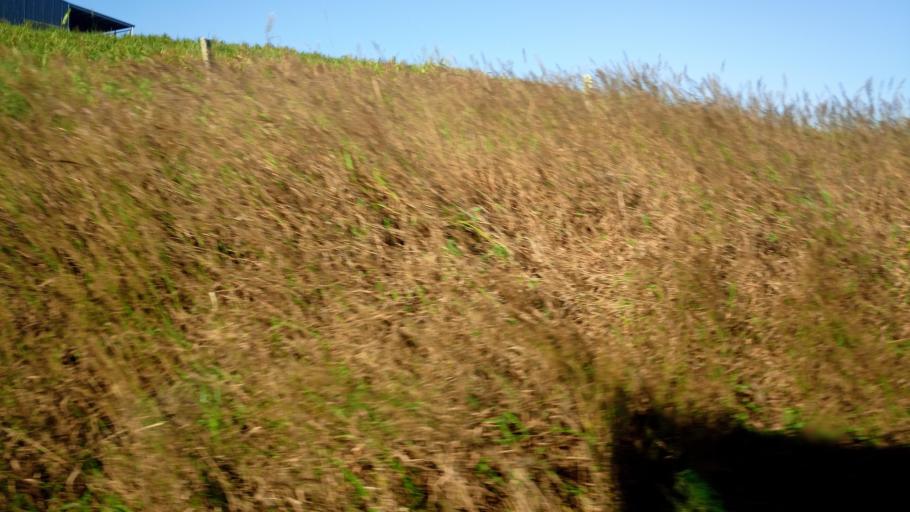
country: AU
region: Queensland
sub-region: Tablelands
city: Ravenshoe
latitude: -17.5380
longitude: 145.6780
